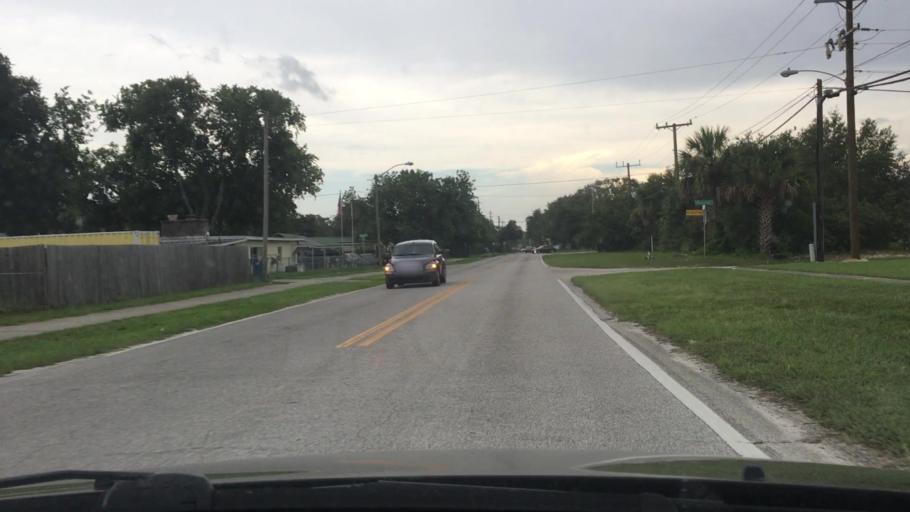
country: US
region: Florida
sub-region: Volusia County
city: Holly Hill
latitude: 29.2335
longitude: -81.0650
